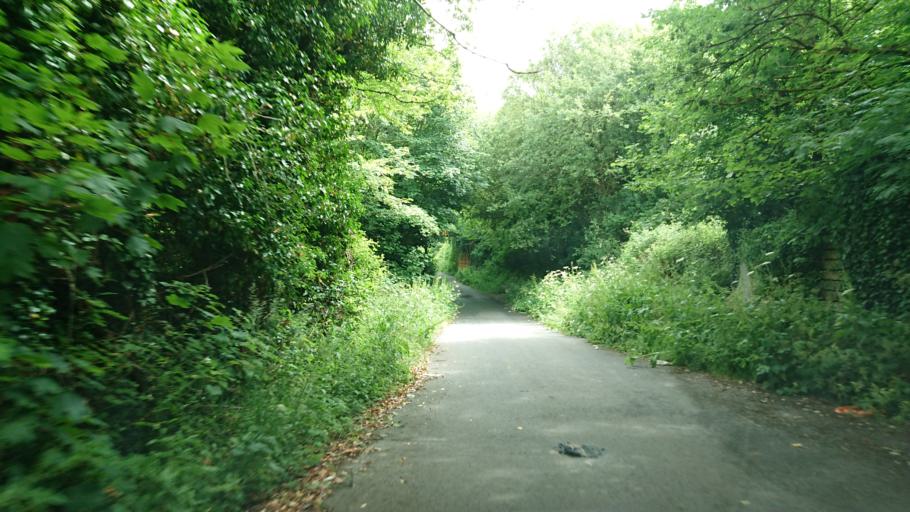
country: IE
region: Munster
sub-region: Waterford
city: Waterford
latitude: 52.2740
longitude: -7.1476
